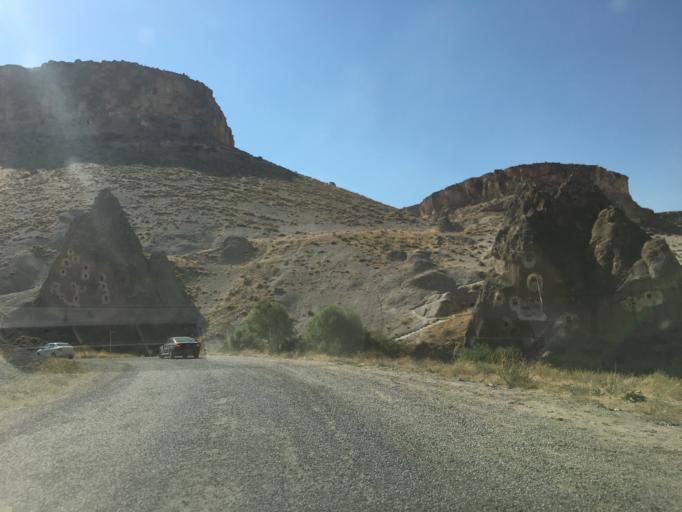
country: TR
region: Kayseri
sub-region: Yesilhisar
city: Yesilhisar
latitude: 38.3451
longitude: 34.9635
